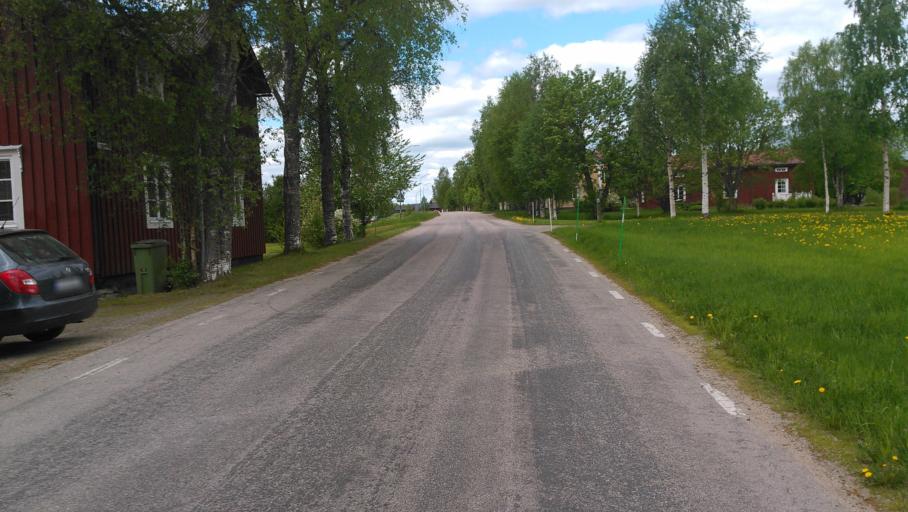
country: SE
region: Vaesterbotten
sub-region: Umea Kommun
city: Roback
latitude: 63.8641
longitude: 20.0833
